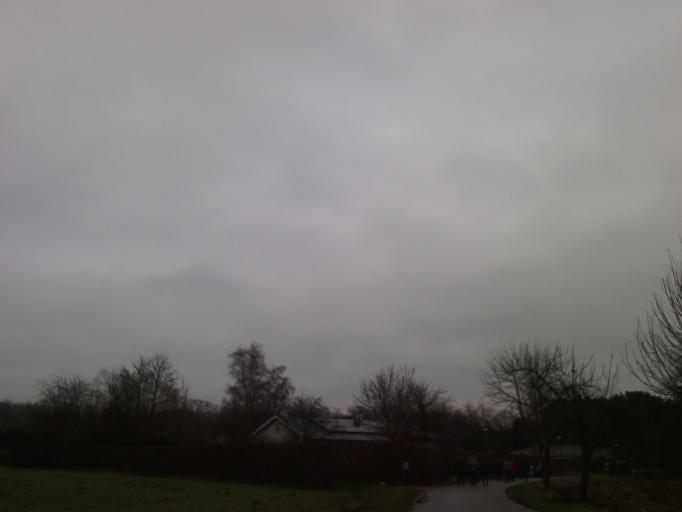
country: BE
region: Flanders
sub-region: Provincie Oost-Vlaanderen
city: Berlare
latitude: 51.0481
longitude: 3.9877
